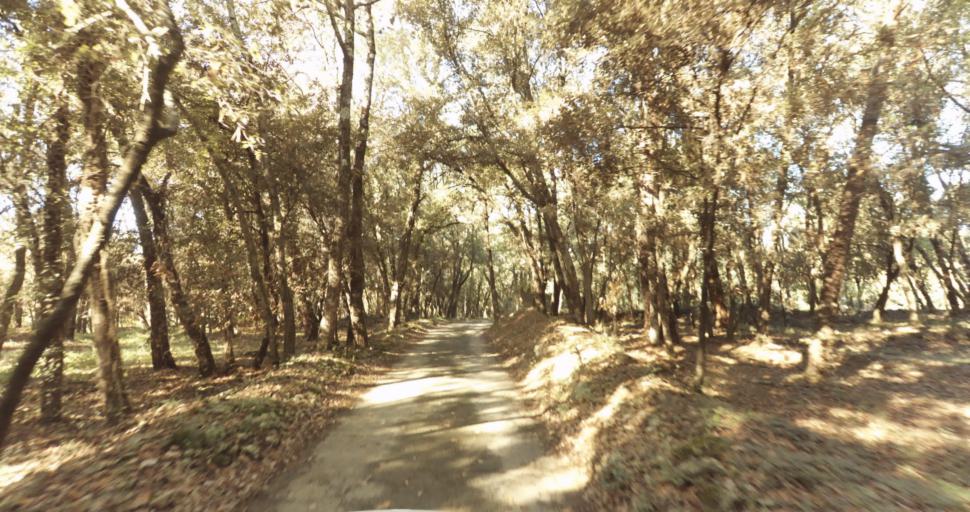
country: FR
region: Provence-Alpes-Cote d'Azur
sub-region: Departement des Alpes-Maritimes
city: Vence
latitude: 43.7098
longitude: 7.1044
